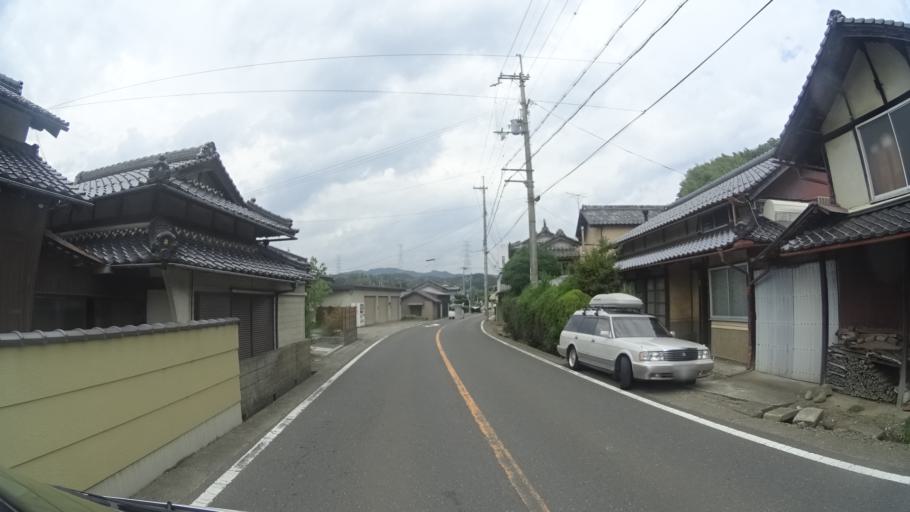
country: JP
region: Kyoto
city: Ayabe
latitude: 35.3413
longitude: 135.2166
